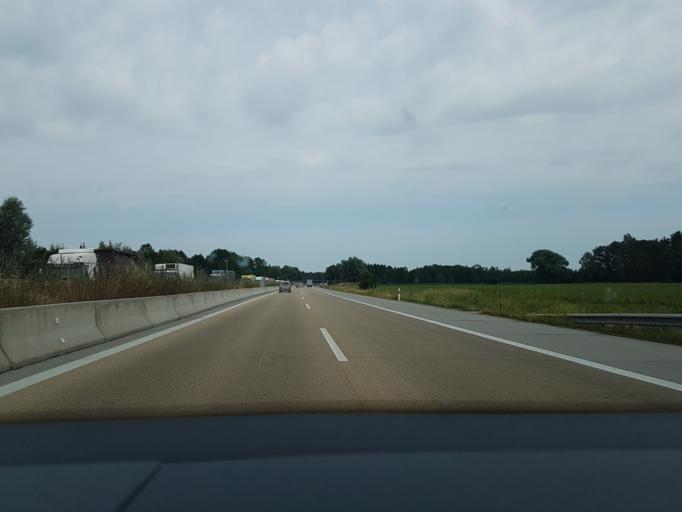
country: DE
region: Bavaria
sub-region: Upper Bavaria
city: Raubling
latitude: 47.7720
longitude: 12.0972
